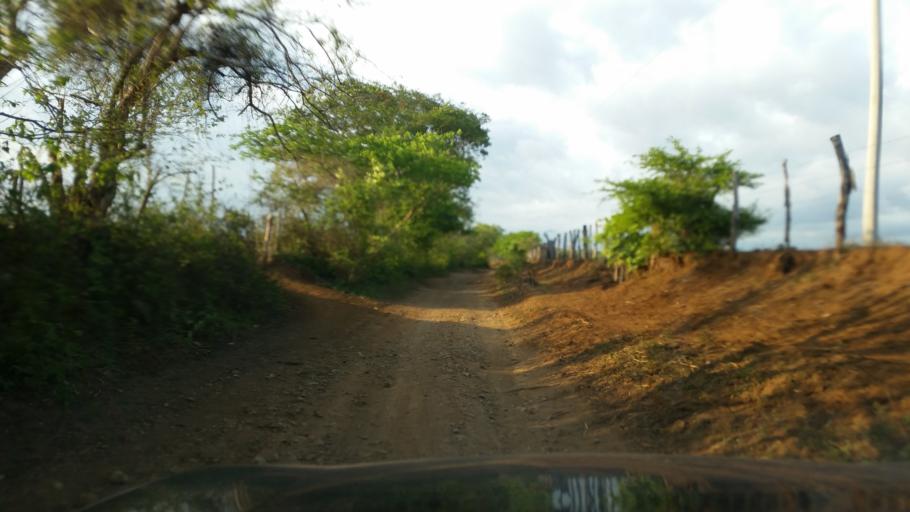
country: NI
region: Managua
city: Masachapa
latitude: 11.7899
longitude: -86.4706
